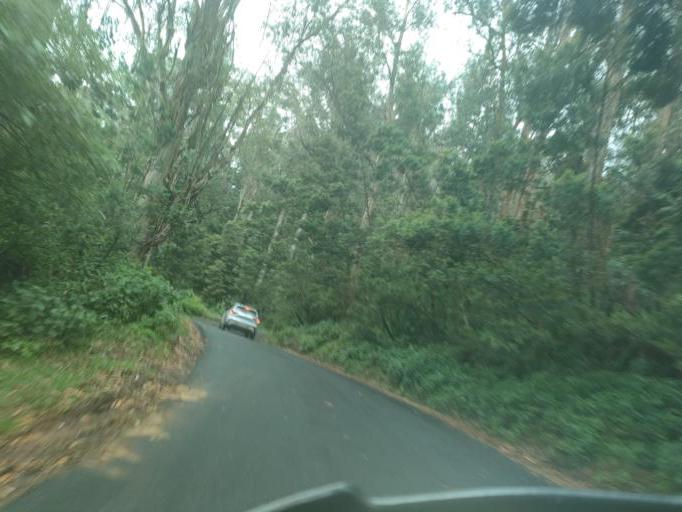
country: IN
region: Tamil Nadu
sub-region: Dindigul
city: Kodaikanal
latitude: 10.2422
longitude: 77.3586
